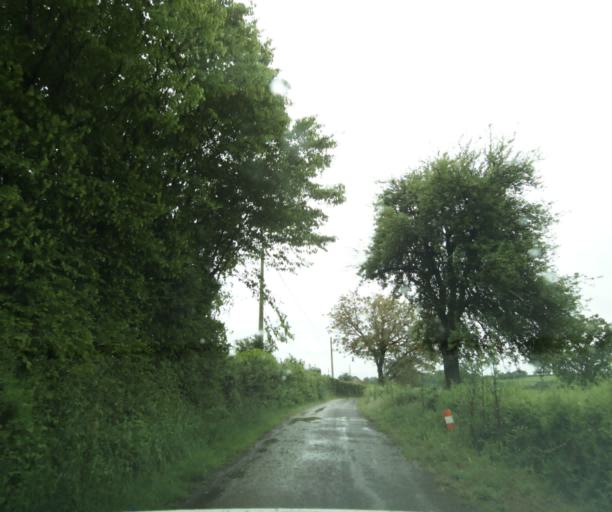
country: FR
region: Bourgogne
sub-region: Departement de Saone-et-Loire
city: Charolles
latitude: 46.4933
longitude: 4.3552
